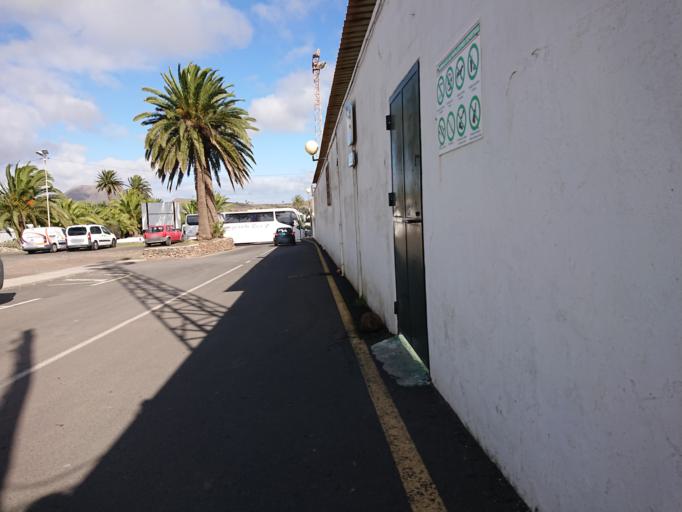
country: ES
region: Canary Islands
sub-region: Provincia de Las Palmas
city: Haria
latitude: 29.1409
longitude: -13.5059
